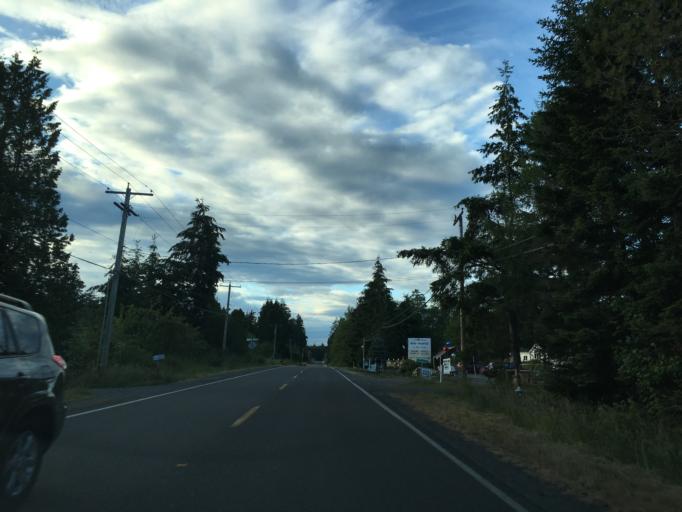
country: US
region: Washington
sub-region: Whatcom County
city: Blaine
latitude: 48.9634
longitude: -122.7299
